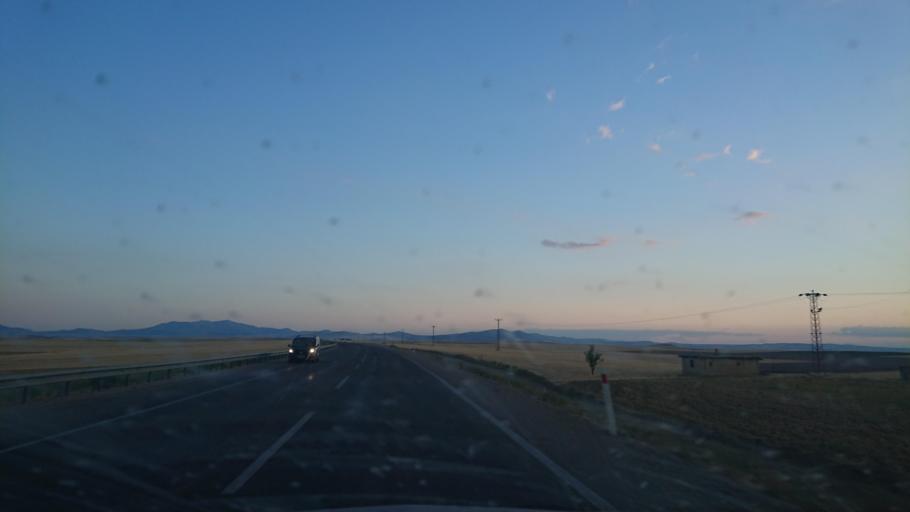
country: TR
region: Aksaray
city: Balci
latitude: 38.9098
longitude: 34.1666
